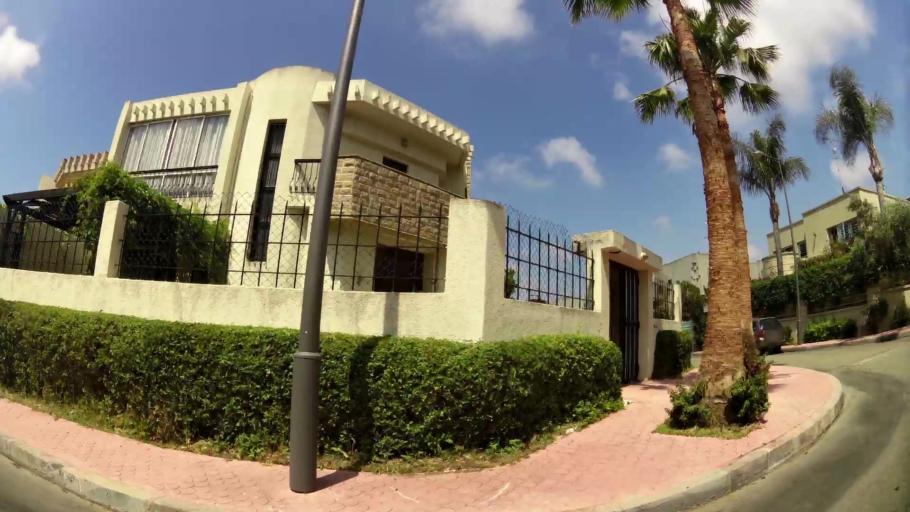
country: MA
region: Rabat-Sale-Zemmour-Zaer
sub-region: Skhirate-Temara
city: Temara
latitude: 33.9574
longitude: -6.8834
